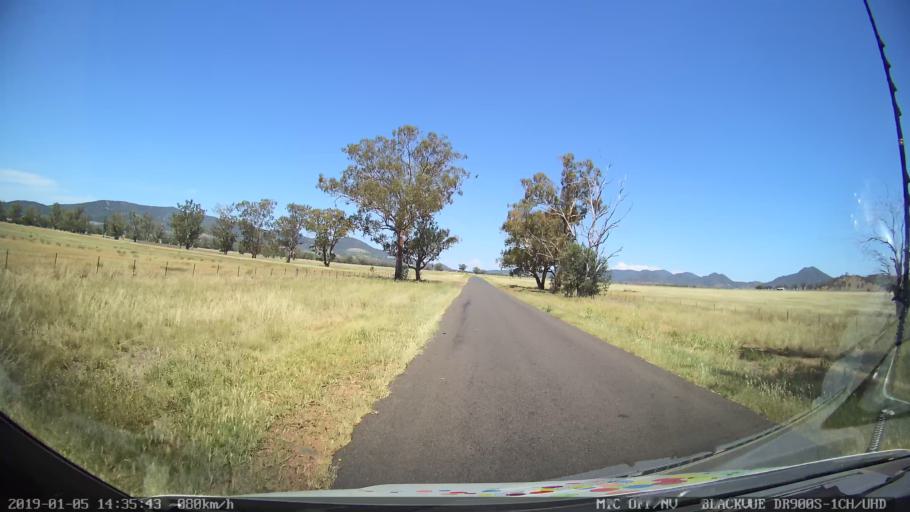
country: AU
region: New South Wales
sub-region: Tamworth Municipality
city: Phillip
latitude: -31.2422
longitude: 150.6537
